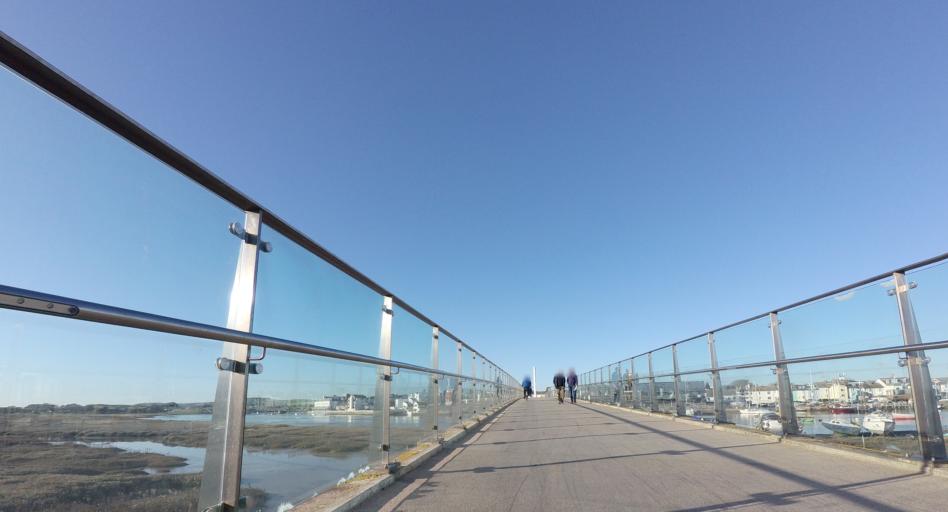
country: GB
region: England
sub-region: West Sussex
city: Shoreham-by-Sea
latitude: 50.8298
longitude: -0.2732
